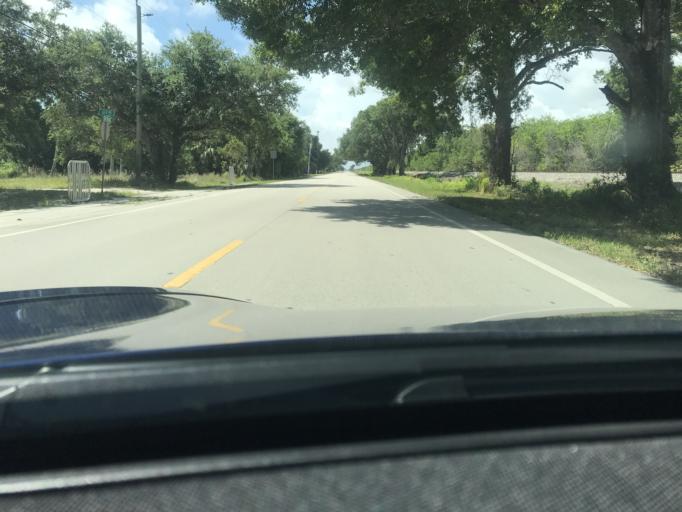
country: US
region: Florida
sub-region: Indian River County
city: Winter Beach
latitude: 27.7050
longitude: -80.4184
